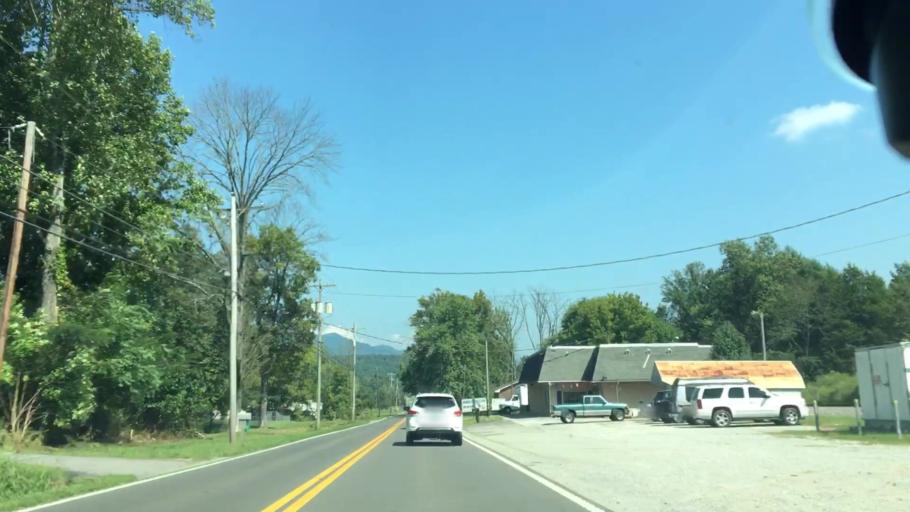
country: US
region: Tennessee
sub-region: Roane County
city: Oliver Springs
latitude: 36.0233
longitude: -84.3713
